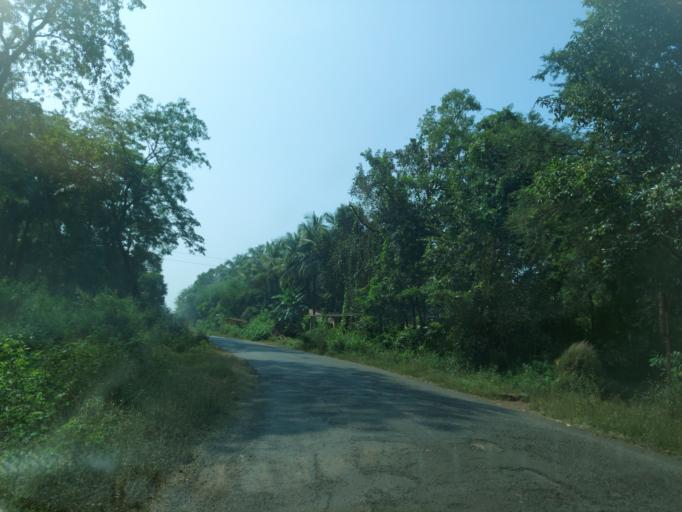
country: IN
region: Maharashtra
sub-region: Sindhudurg
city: Kudal
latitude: 15.9866
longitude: 73.6691
